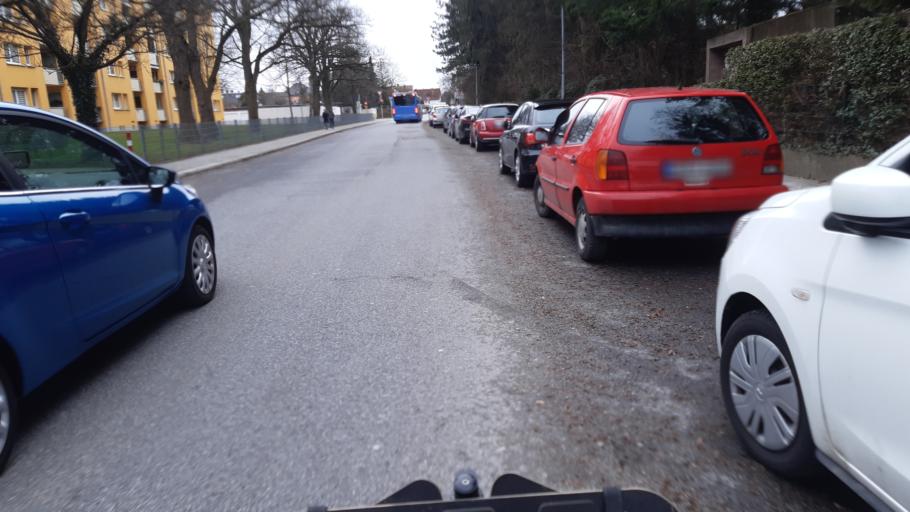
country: DE
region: Bavaria
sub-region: Upper Bavaria
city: Oberschleissheim
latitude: 48.2095
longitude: 11.5559
